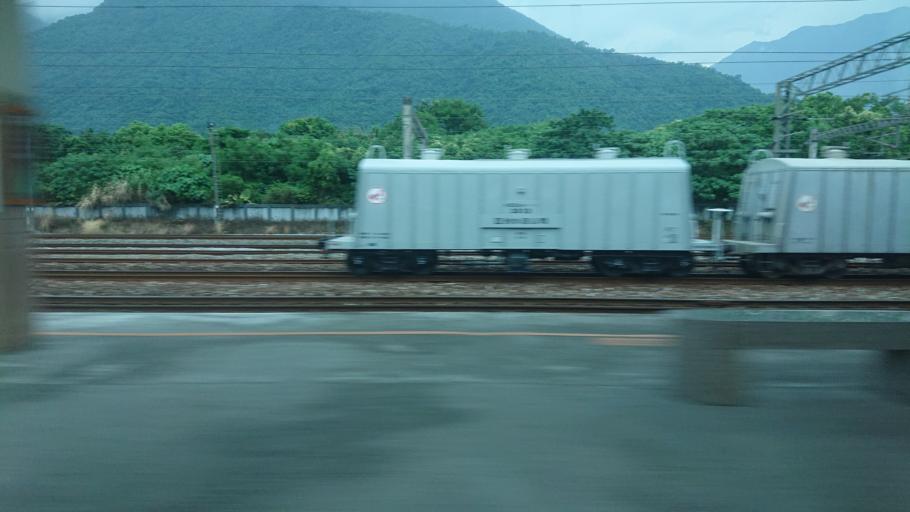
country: TW
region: Taiwan
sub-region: Hualien
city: Hualian
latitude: 24.1273
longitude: 121.6403
